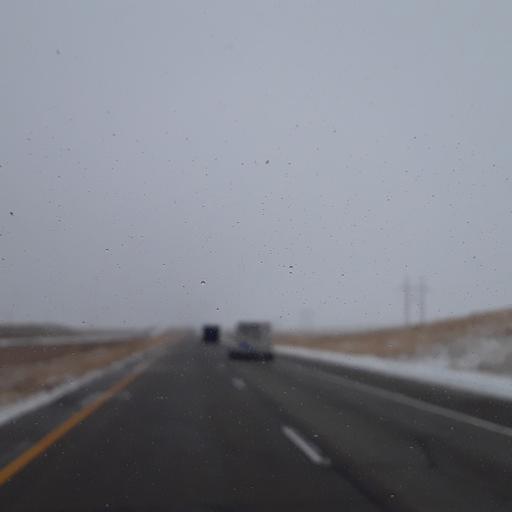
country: US
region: Colorado
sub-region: Logan County
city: Sterling
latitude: 40.7646
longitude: -102.9524
